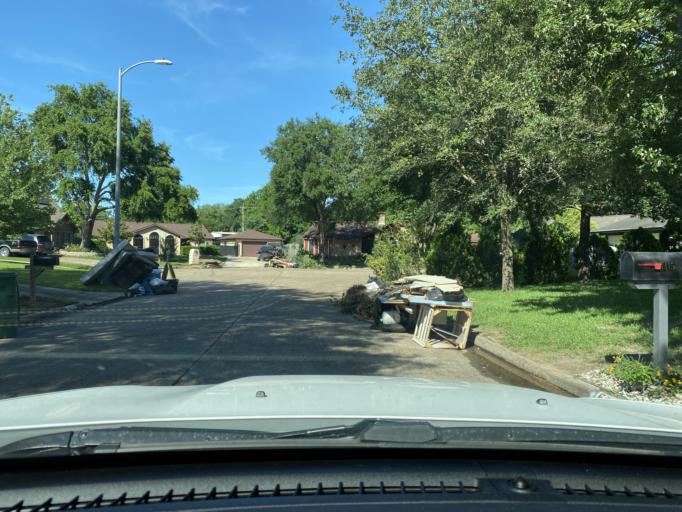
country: US
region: Texas
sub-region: Harris County
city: Hudson
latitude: 29.8770
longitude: -95.4859
